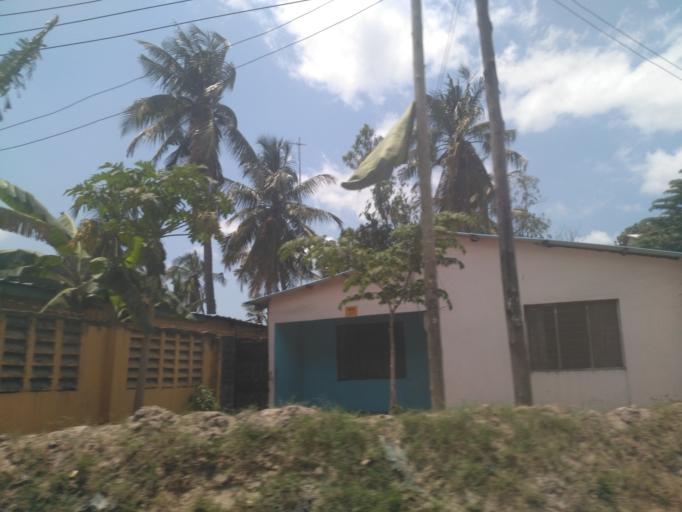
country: TZ
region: Dar es Salaam
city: Dar es Salaam
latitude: -6.8862
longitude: 39.2744
